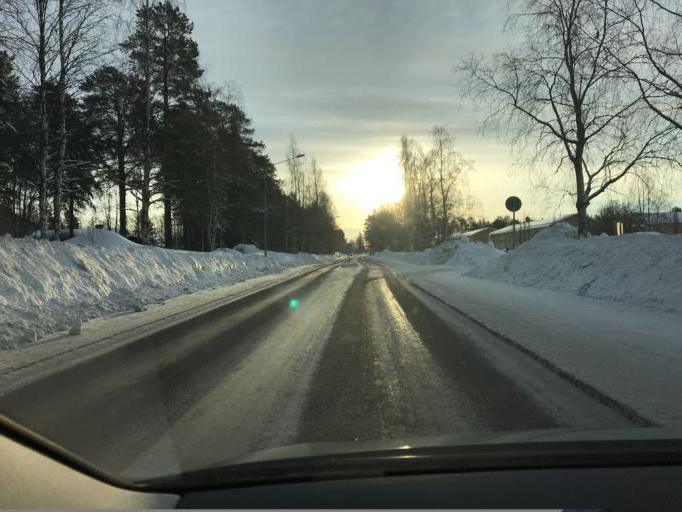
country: SE
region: Norrbotten
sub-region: Lulea Kommun
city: Bergnaset
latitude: 65.6083
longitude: 22.1046
